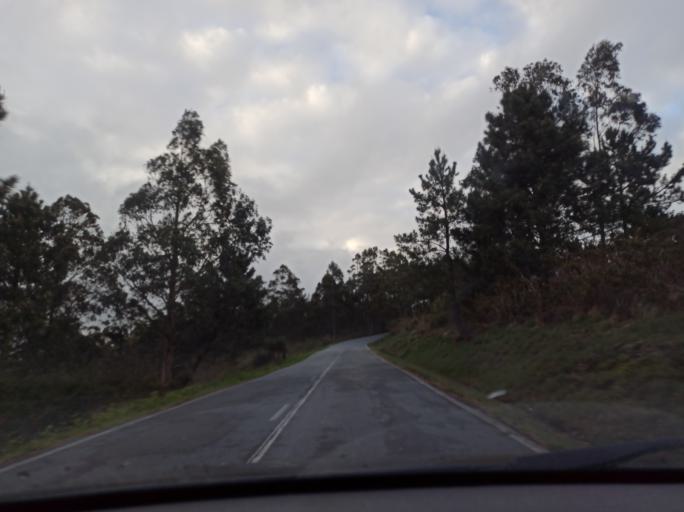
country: ES
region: Galicia
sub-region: Provincia da Coruna
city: Culleredo
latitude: 43.3035
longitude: -8.4299
